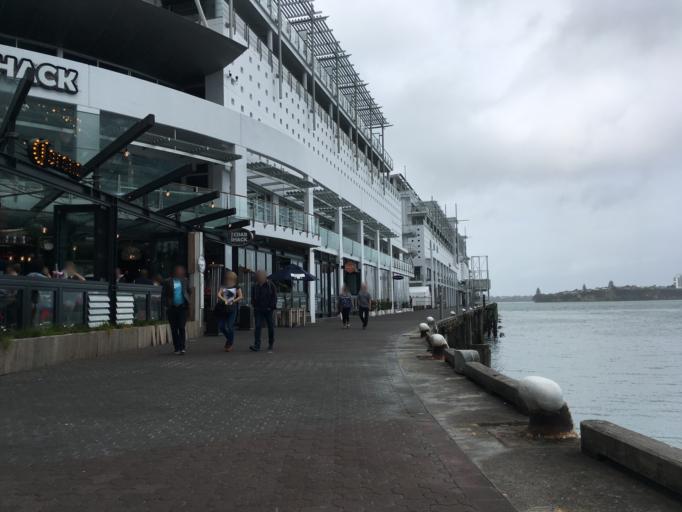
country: NZ
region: Auckland
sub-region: Auckland
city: Auckland
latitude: -36.8421
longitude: 174.7651
